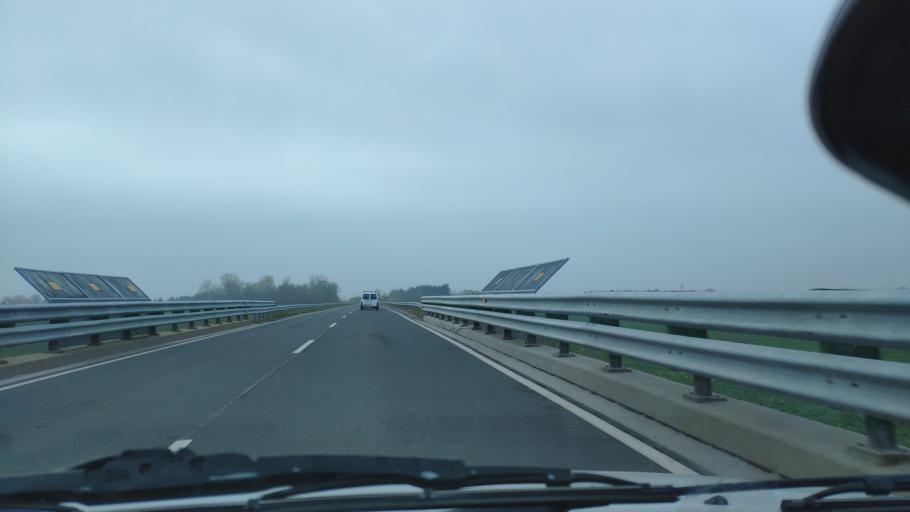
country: HU
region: Zala
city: Zalakomar
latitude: 46.5354
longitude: 17.1929
